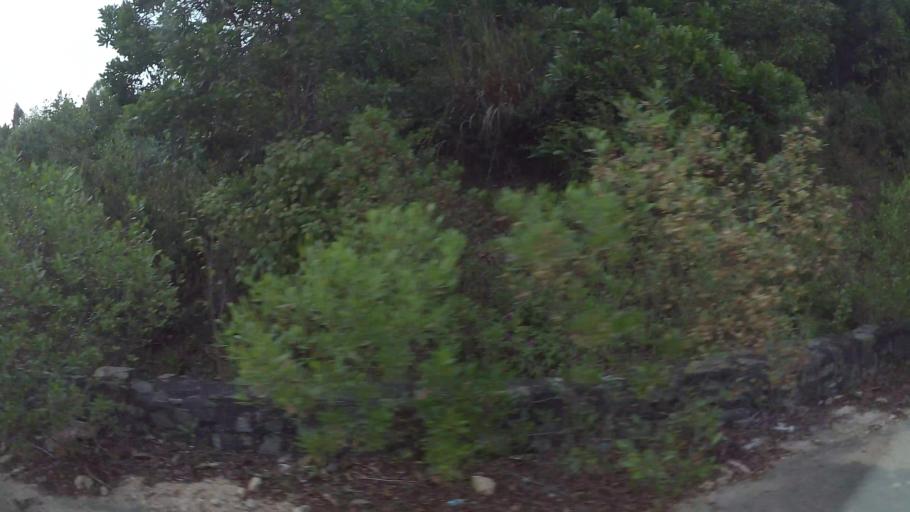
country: VN
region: Da Nang
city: Lien Chieu
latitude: 16.0622
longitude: 108.1152
